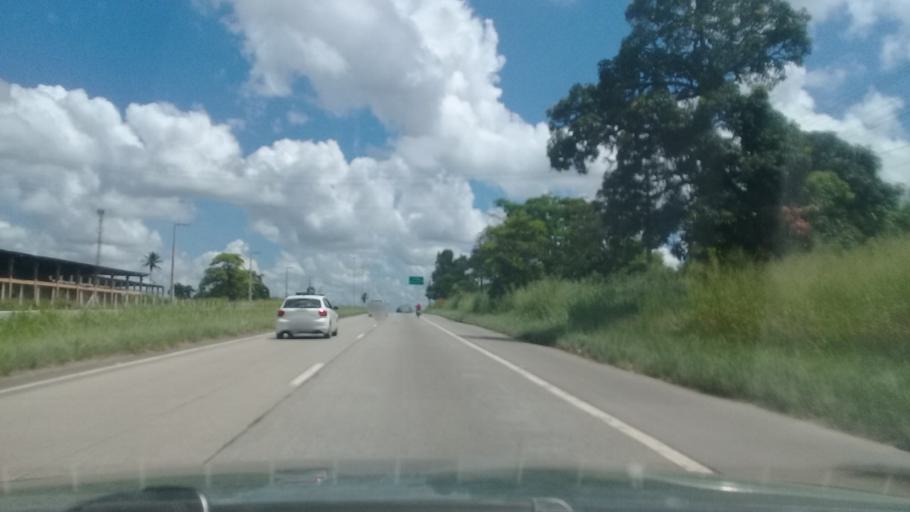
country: BR
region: Pernambuco
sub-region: Carpina
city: Carpina
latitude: -7.9191
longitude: -35.1627
